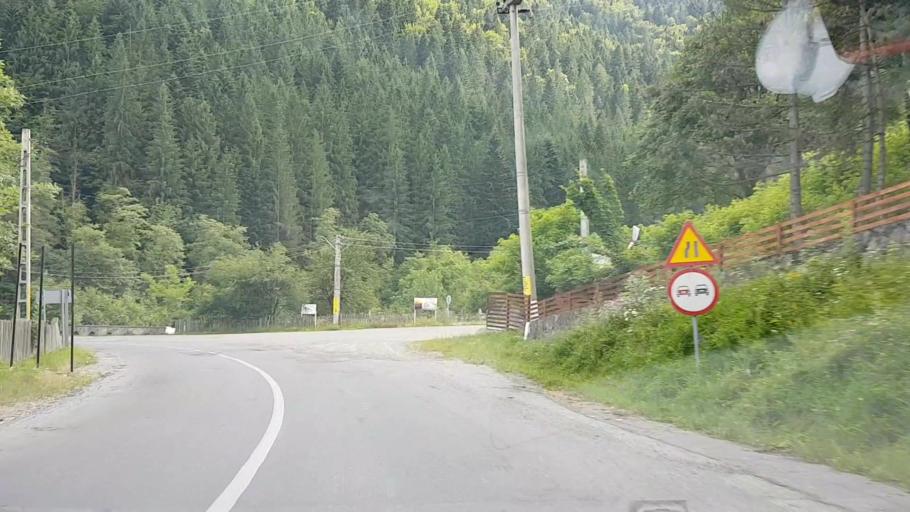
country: RO
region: Neamt
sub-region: Comuna Bicaz
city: Dodeni
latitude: 46.9393
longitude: 26.0832
